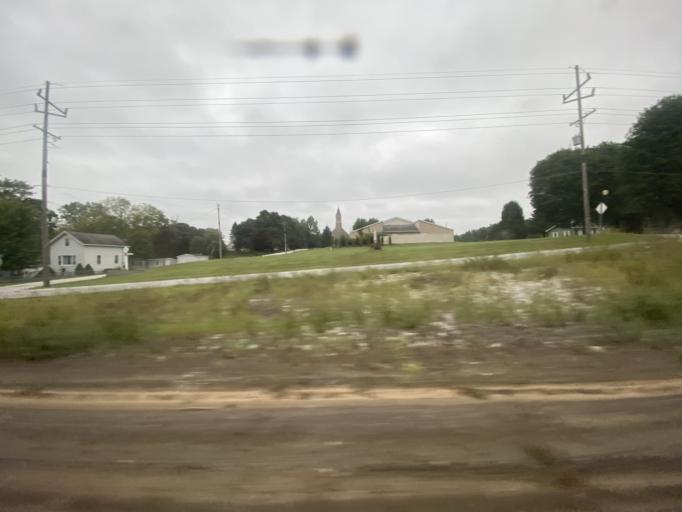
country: US
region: Indiana
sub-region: LaPorte County
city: Westville
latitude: 41.5993
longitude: -86.9039
